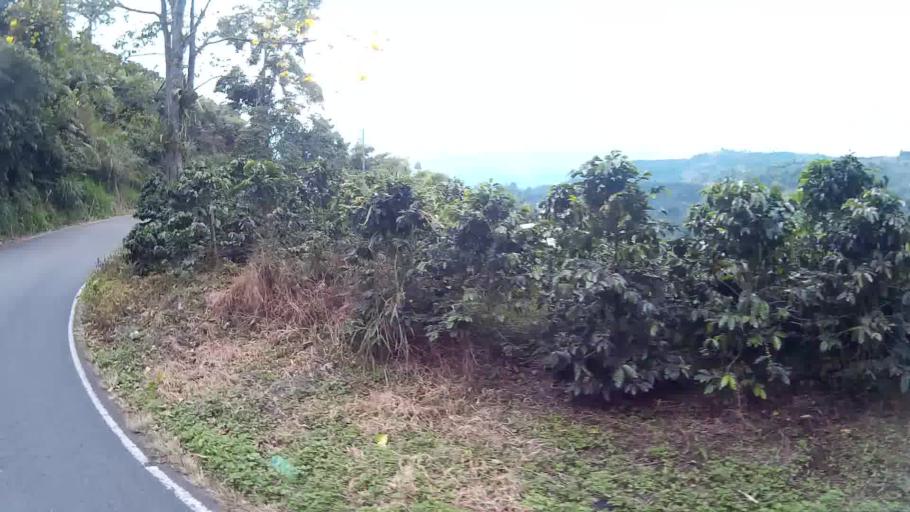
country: CO
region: Risaralda
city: Marsella
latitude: 4.9017
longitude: -75.7396
